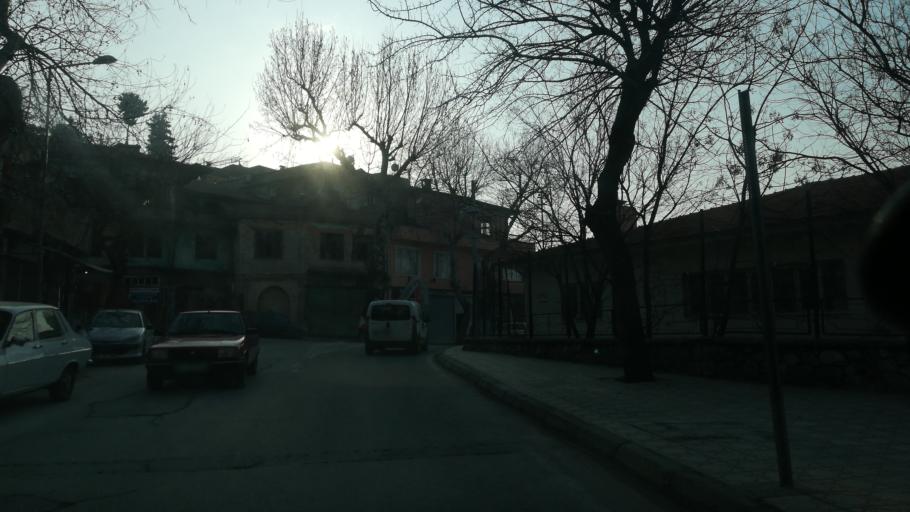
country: TR
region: Kahramanmaras
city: Kahramanmaras
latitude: 37.5846
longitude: 36.9300
